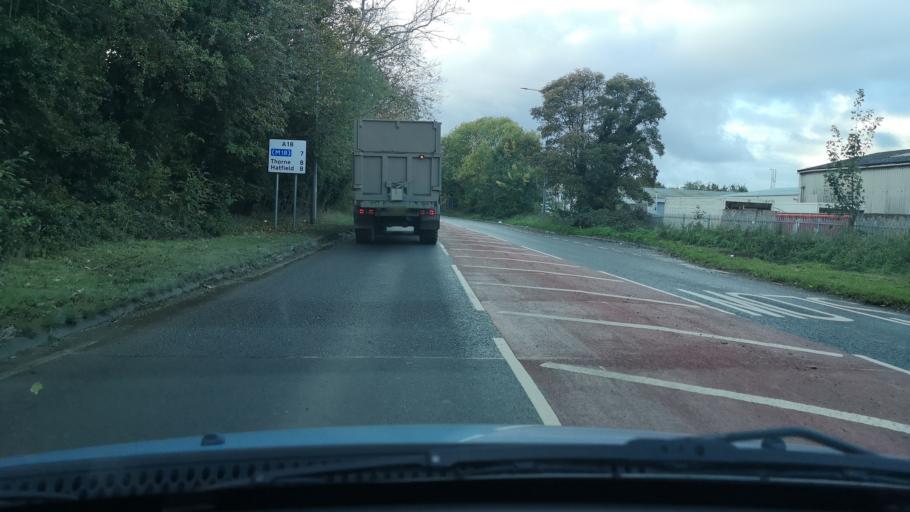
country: GB
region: England
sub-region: North Lincolnshire
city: Crowle
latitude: 53.5860
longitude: -0.8202
